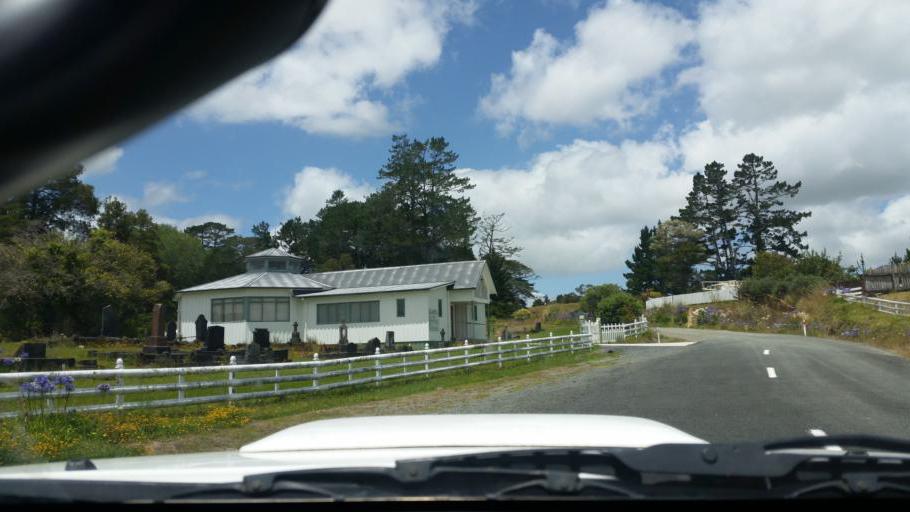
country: NZ
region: Northland
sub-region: Whangarei
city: Ruakaka
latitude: -36.0974
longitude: 174.2432
